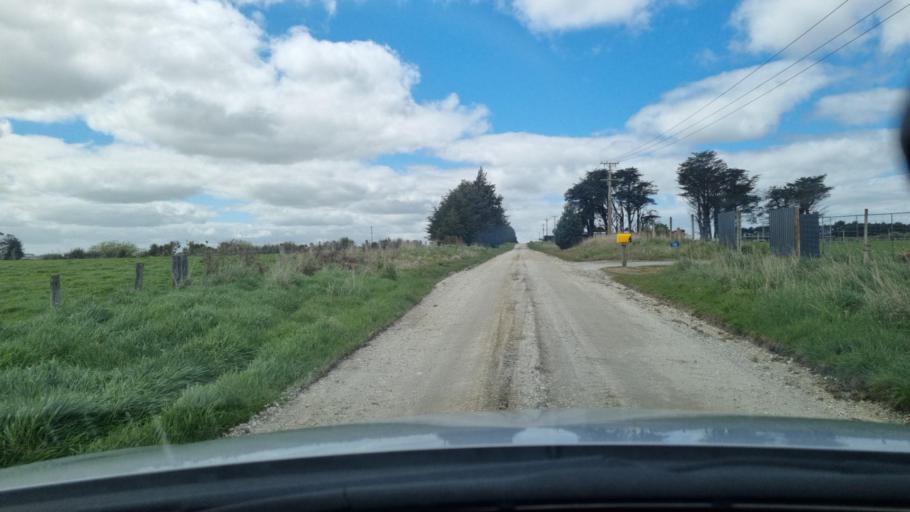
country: NZ
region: Southland
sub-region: Invercargill City
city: Invercargill
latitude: -46.4506
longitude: 168.4014
